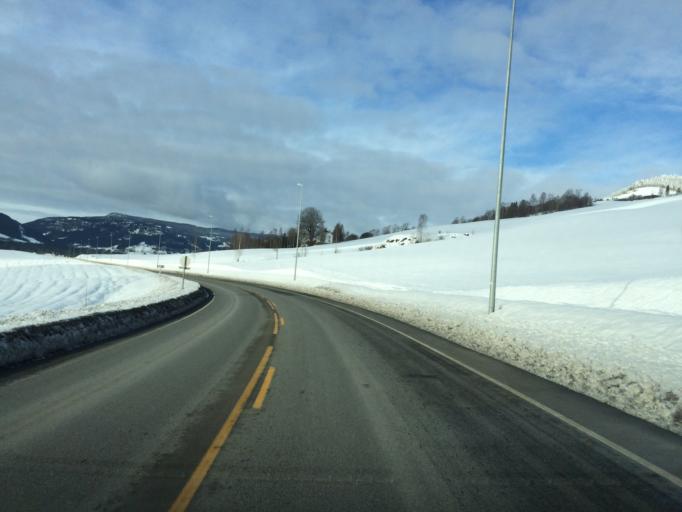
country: NO
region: Oppland
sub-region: Gausdal
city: Segalstad bru
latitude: 61.2203
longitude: 10.2674
